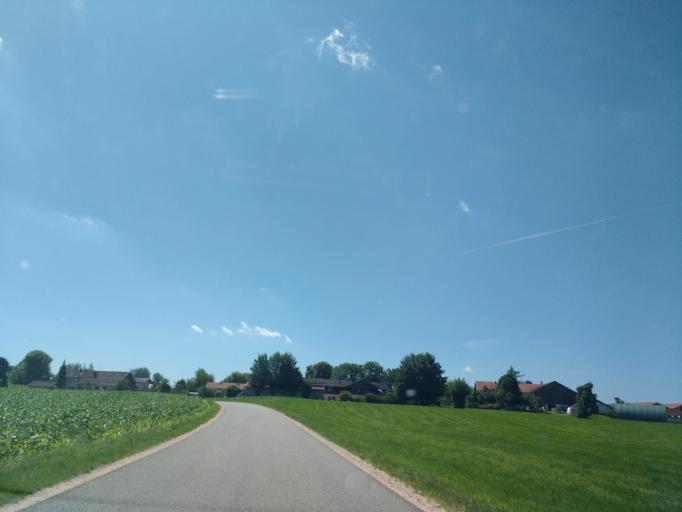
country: DE
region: Bavaria
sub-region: Upper Bavaria
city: Obing
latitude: 48.0168
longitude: 12.4409
